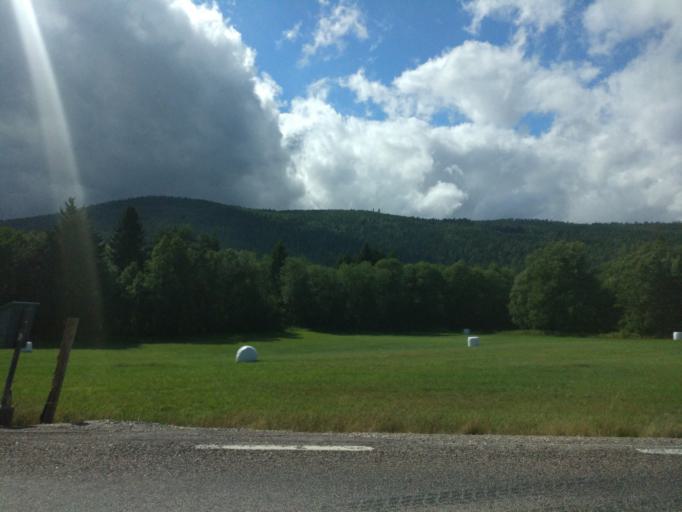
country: SE
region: Vaermland
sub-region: Hagfors Kommun
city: Ekshaerad
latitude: 60.3635
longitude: 13.3106
